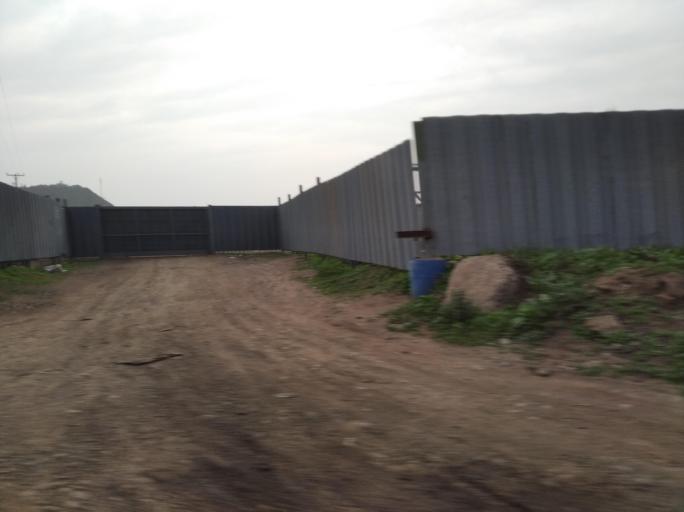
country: CL
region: Santiago Metropolitan
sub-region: Provincia de Chacabuco
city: Lampa
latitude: -33.3595
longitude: -70.8024
